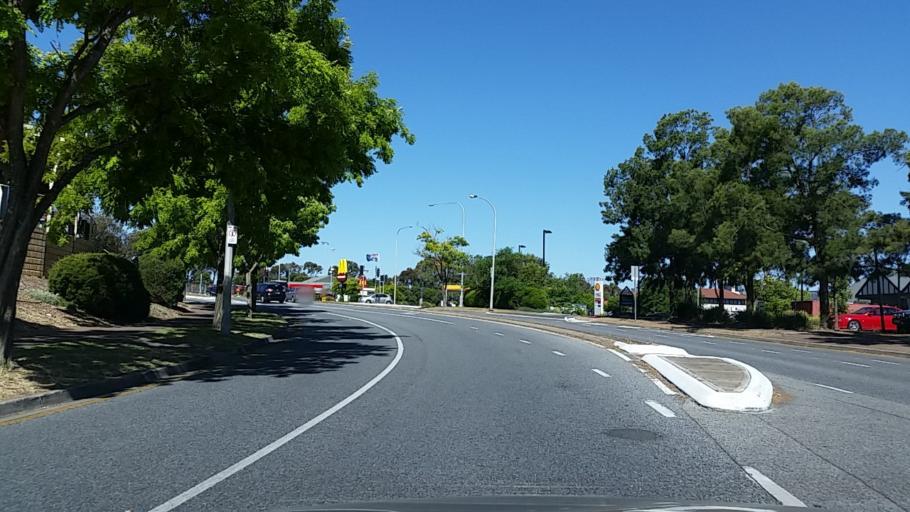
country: AU
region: South Australia
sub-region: Tea Tree Gully
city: Golden Grove
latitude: -34.7891
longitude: 138.6958
